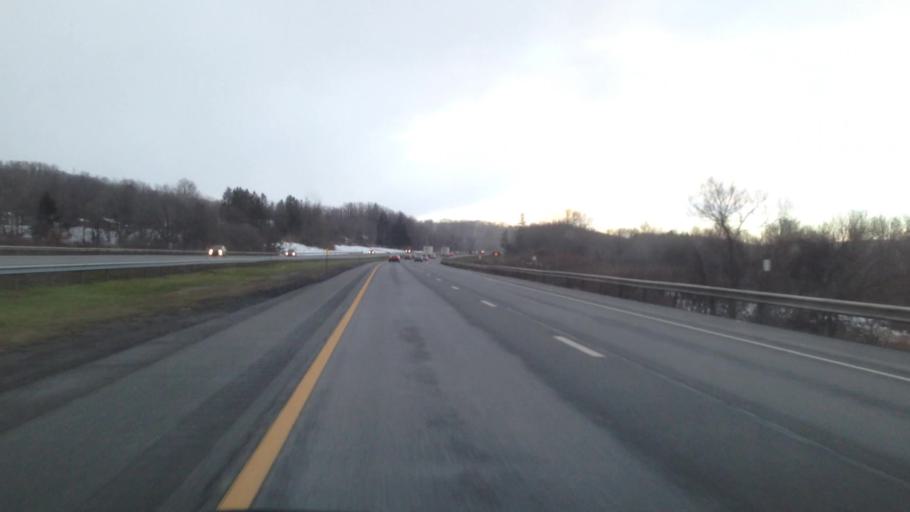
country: US
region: New York
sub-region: Herkimer County
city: Little Falls
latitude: 43.0067
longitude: -74.7796
